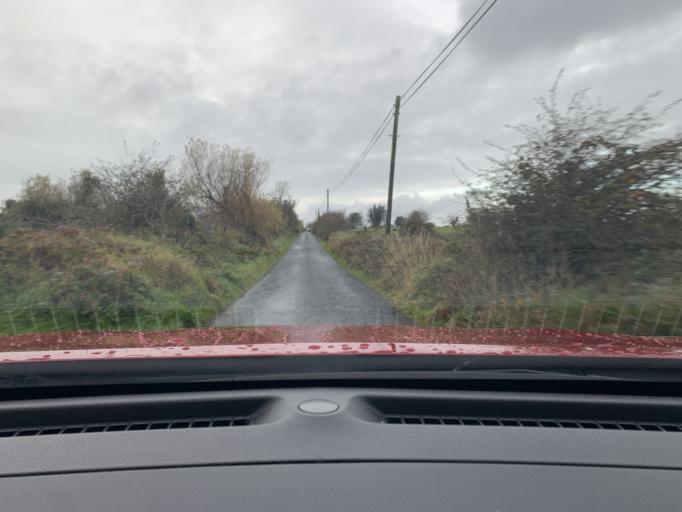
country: IE
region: Connaught
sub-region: Roscommon
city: Ballaghaderreen
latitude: 53.9656
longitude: -8.5503
